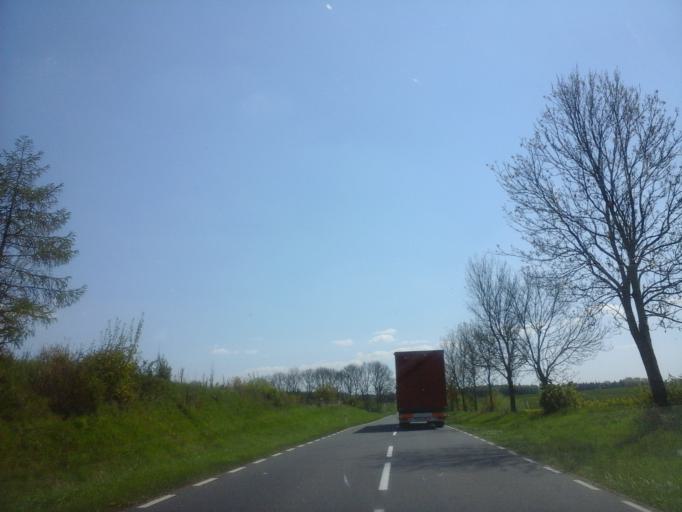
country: PL
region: West Pomeranian Voivodeship
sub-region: Powiat choszczenski
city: Bierzwnik
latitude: 53.1001
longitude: 15.6320
